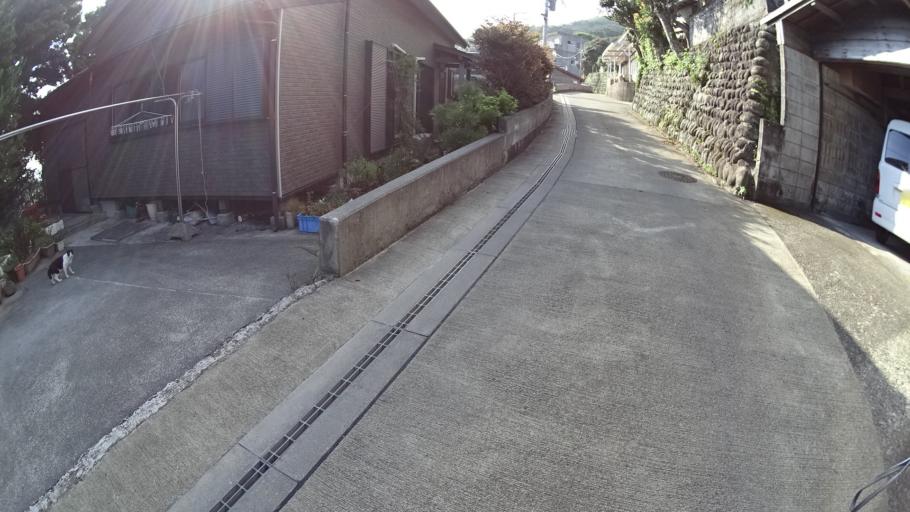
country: JP
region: Shizuoka
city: Shimoda
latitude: 34.5294
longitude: 139.2773
